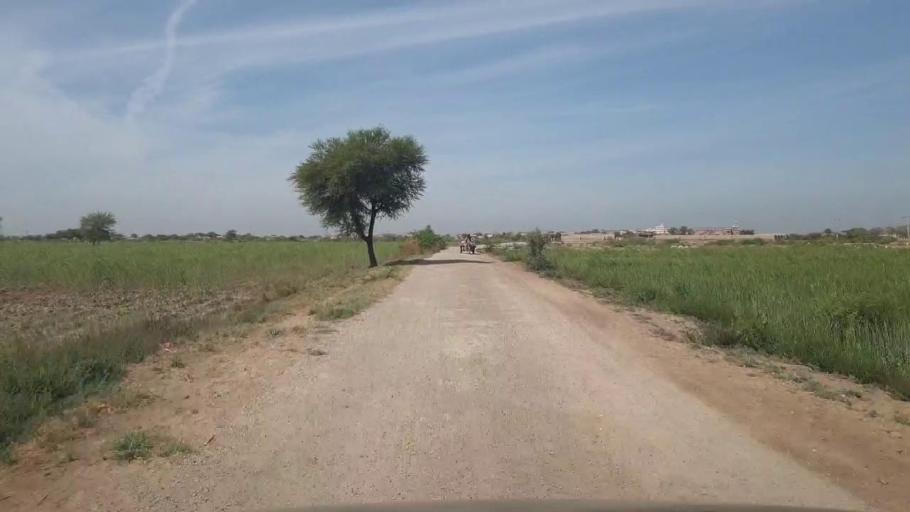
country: PK
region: Sindh
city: Umarkot
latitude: 25.3522
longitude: 69.5940
